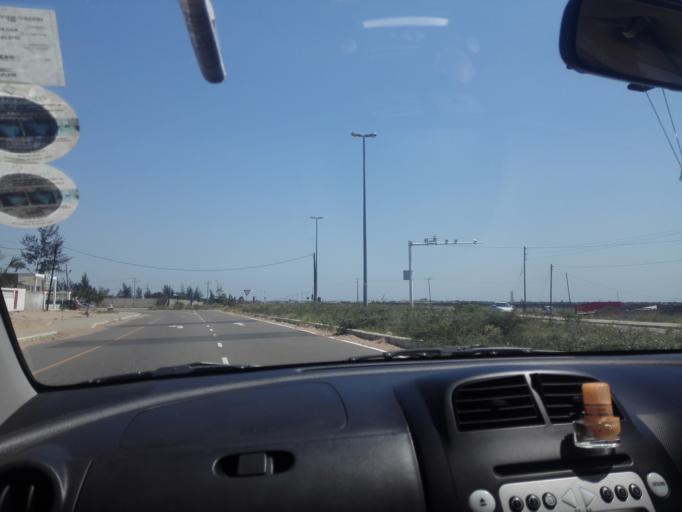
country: MZ
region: Maputo City
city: Maputo
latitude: -25.8492
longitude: 32.6713
